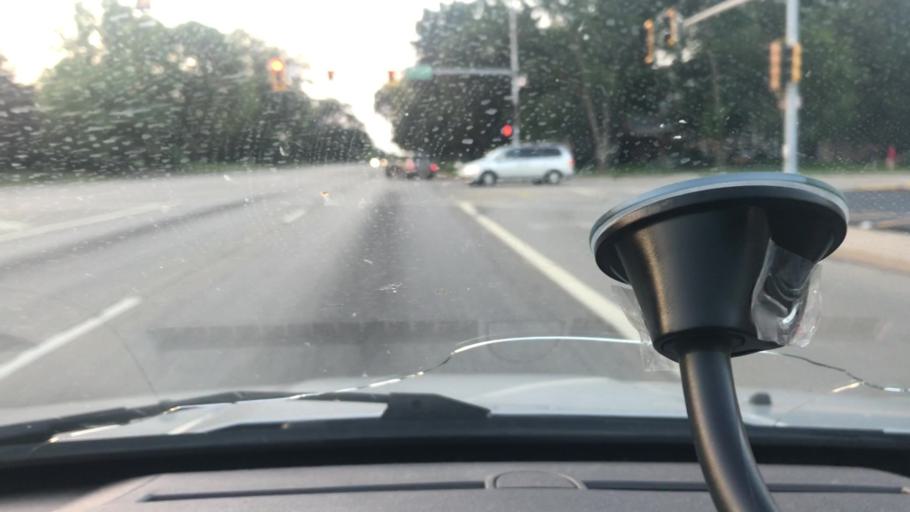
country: US
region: Illinois
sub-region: Tazewell County
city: Pekin
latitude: 40.5820
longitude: -89.6410
